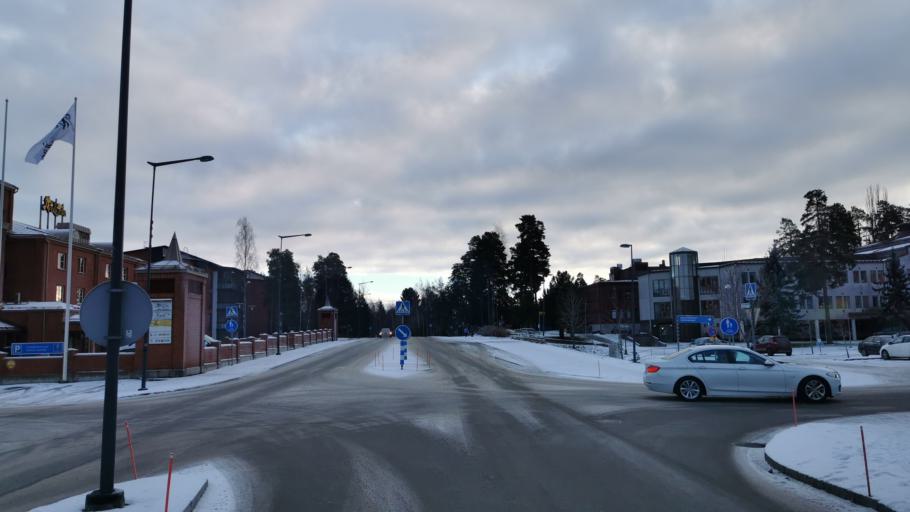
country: FI
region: Ostrobothnia
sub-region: Vaasa
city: Korsholm
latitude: 63.1122
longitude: 21.6778
